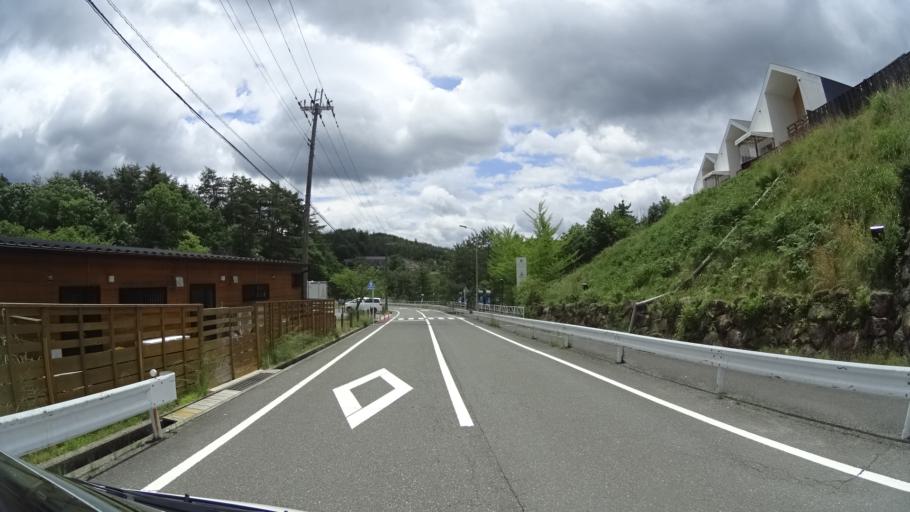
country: JP
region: Hyogo
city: Sasayama
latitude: 35.0319
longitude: 135.3982
